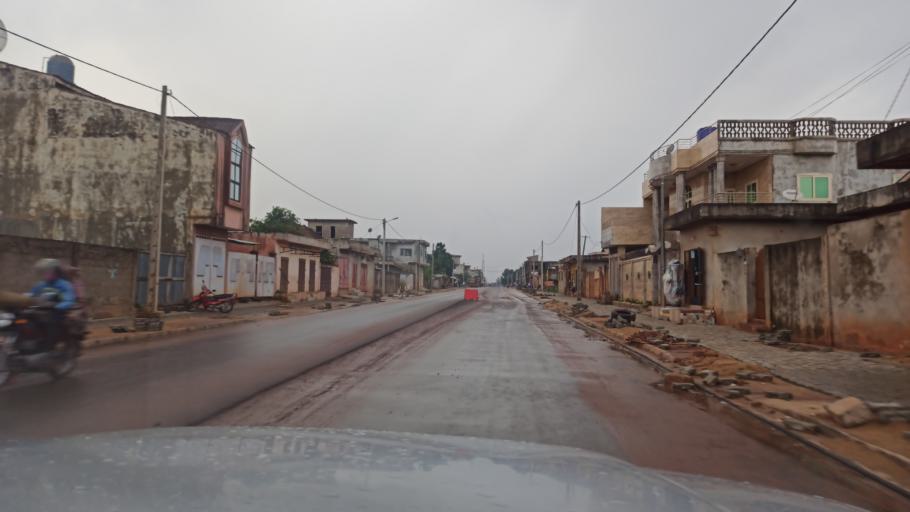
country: BJ
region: Queme
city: Porto-Novo
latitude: 6.4934
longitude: 2.6465
